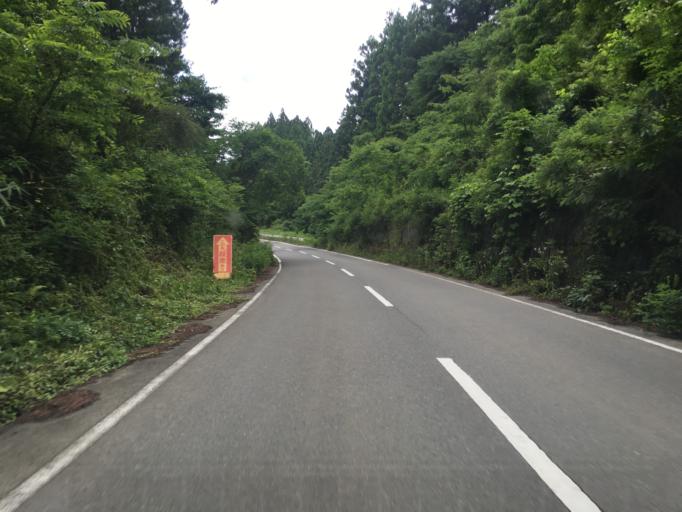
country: JP
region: Fukushima
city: Namie
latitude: 37.6904
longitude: 140.8871
